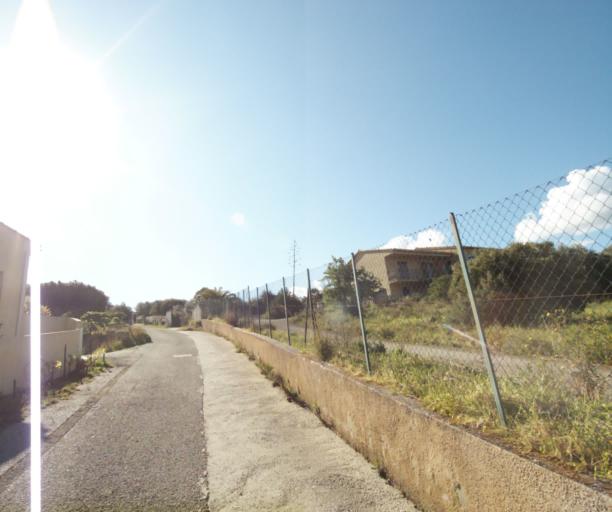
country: FR
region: Corsica
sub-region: Departement de la Corse-du-Sud
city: Propriano
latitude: 41.6682
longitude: 8.9009
